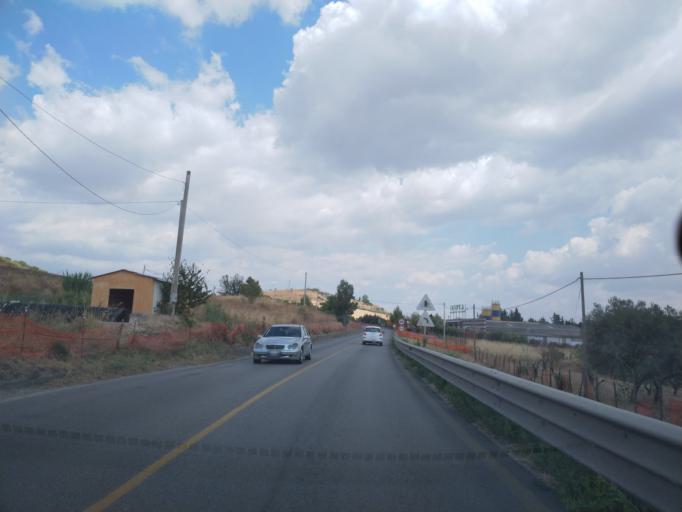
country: IT
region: Sicily
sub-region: Provincia di Caltanissetta
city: San Cataldo
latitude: 37.4549
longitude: 13.9877
